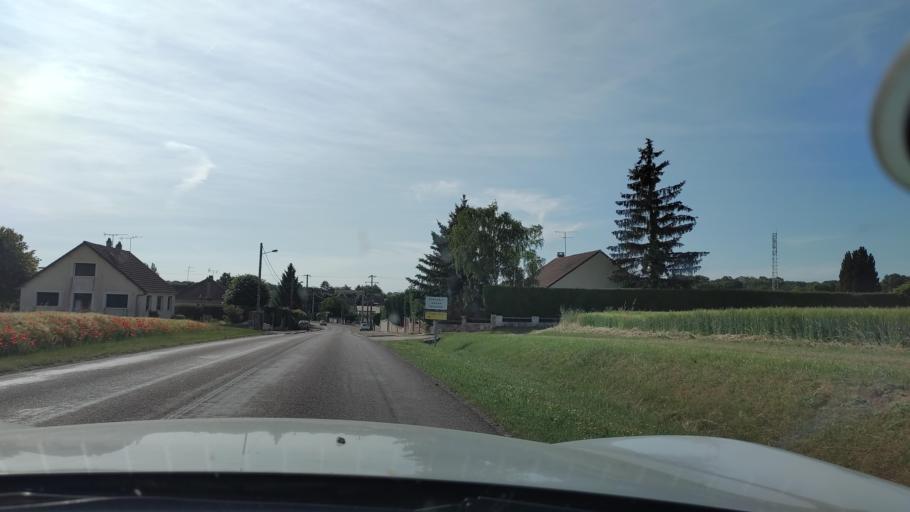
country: FR
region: Champagne-Ardenne
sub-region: Departement de l'Aube
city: Nogent-sur-Seine
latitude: 48.4775
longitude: 3.5507
